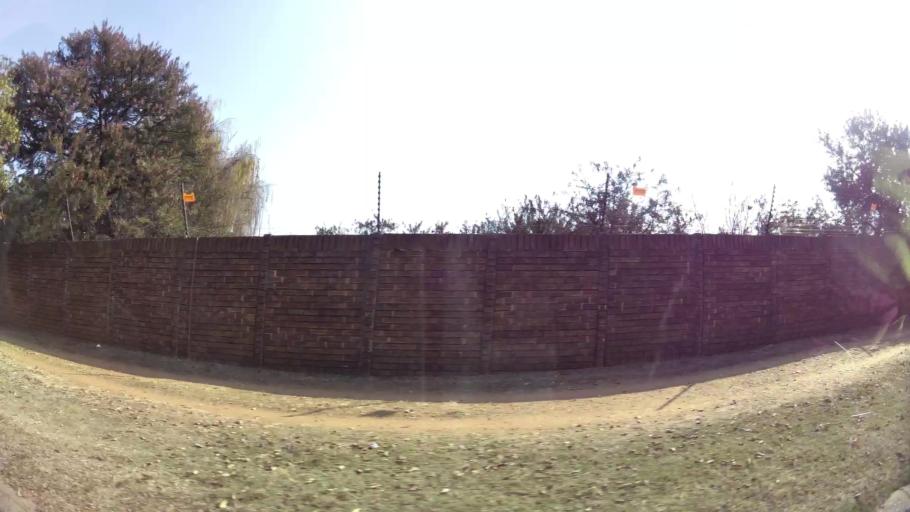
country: ZA
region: Gauteng
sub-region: City of Tshwane Metropolitan Municipality
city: Pretoria
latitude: -25.7798
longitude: 28.3663
